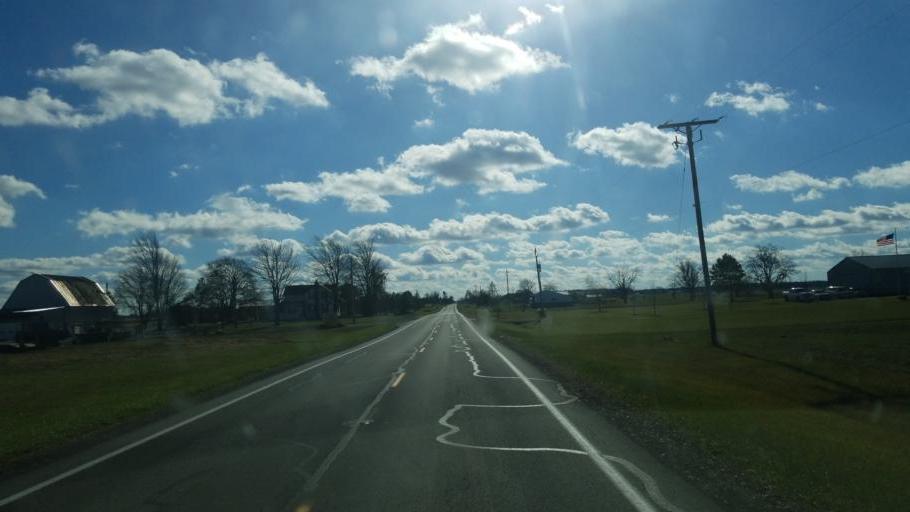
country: US
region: Ohio
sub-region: Hardin County
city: Kenton
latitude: 40.6089
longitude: -83.5954
